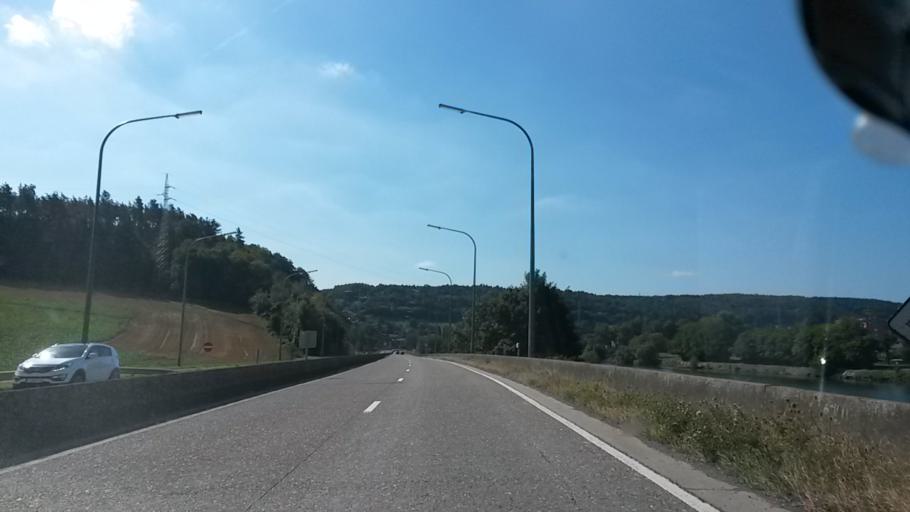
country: BE
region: Wallonia
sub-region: Province de Liege
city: Amay
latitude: 50.5518
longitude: 5.3349
